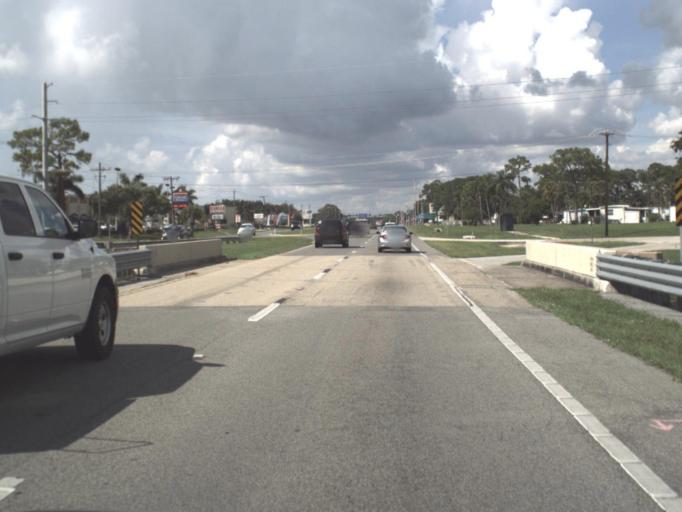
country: US
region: Florida
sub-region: Sarasota County
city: Vamo
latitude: 27.2211
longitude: -82.4912
